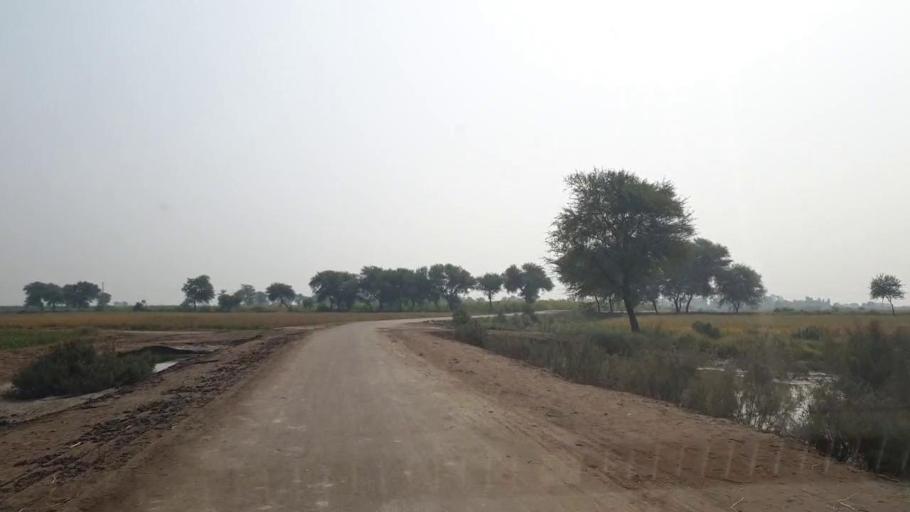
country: PK
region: Sindh
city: Matli
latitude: 25.1298
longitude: 68.7034
